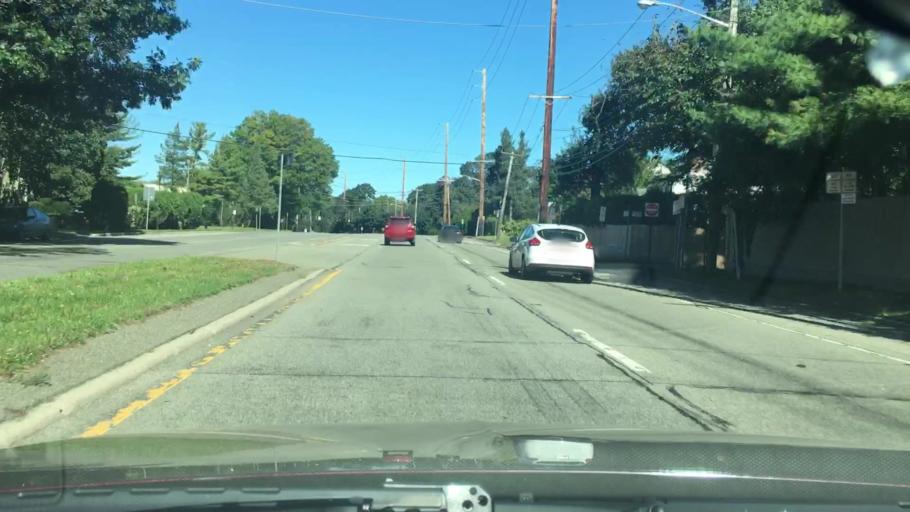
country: US
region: New York
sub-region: Nassau County
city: Roslyn Estates
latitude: 40.8026
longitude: -73.6687
